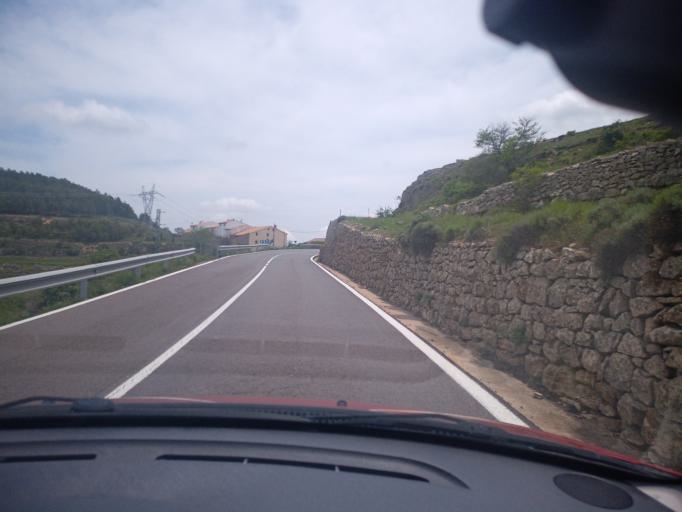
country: ES
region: Valencia
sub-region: Provincia de Castello
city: Ares del Maestre
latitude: 40.4553
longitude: -0.1443
